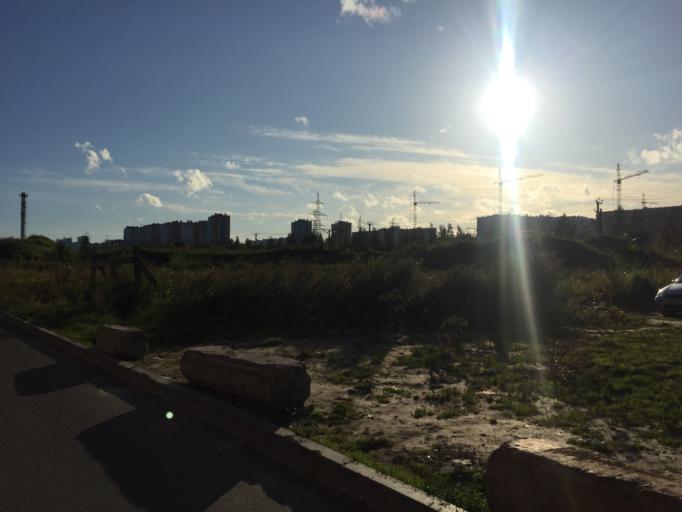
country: RU
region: Leningrad
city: Murino
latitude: 60.0667
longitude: 30.4555
